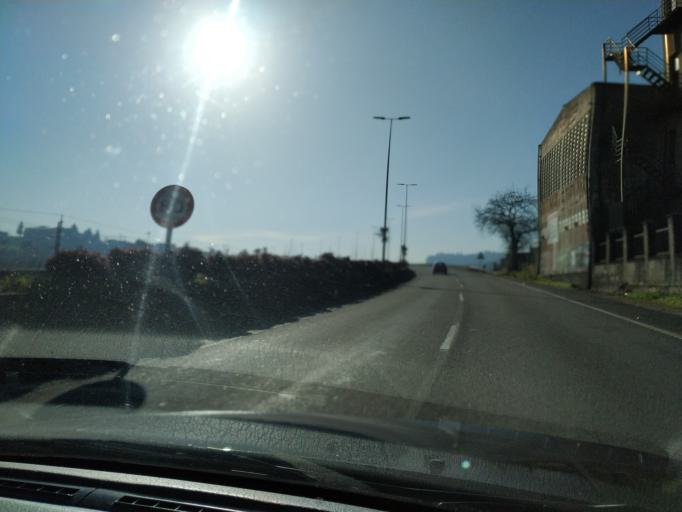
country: ES
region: Galicia
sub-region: Provincia da Coruna
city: Santiago de Compostela
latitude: 42.8654
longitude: -8.5525
